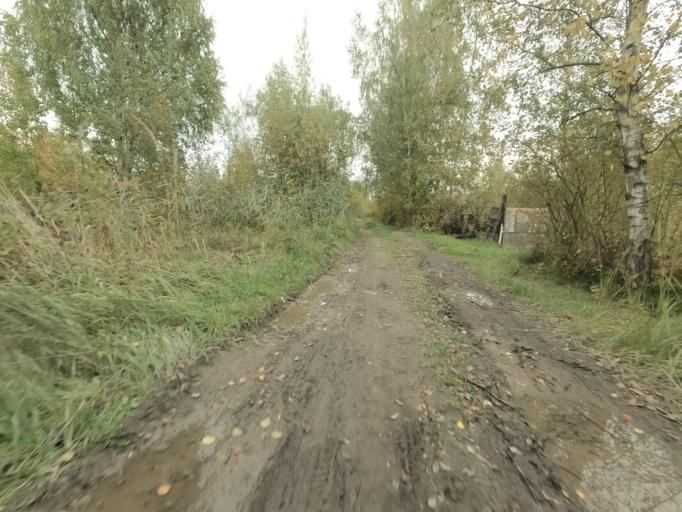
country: RU
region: St.-Petersburg
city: Sapernyy
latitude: 59.7782
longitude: 30.6393
